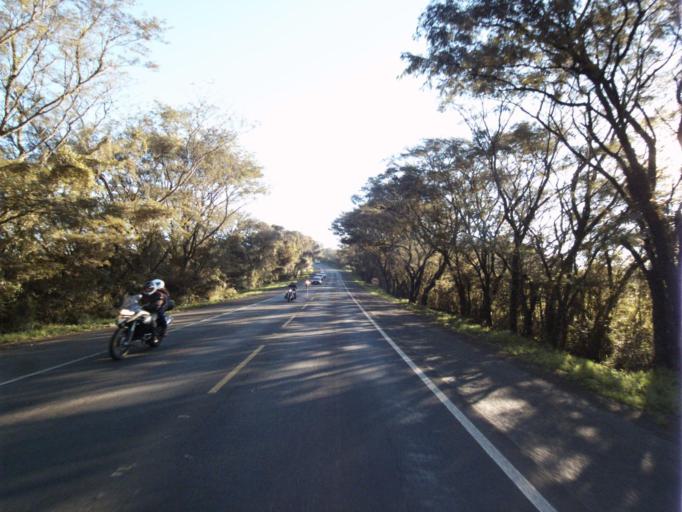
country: BR
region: Santa Catarina
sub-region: Chapeco
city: Chapeco
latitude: -26.8994
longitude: -52.8841
